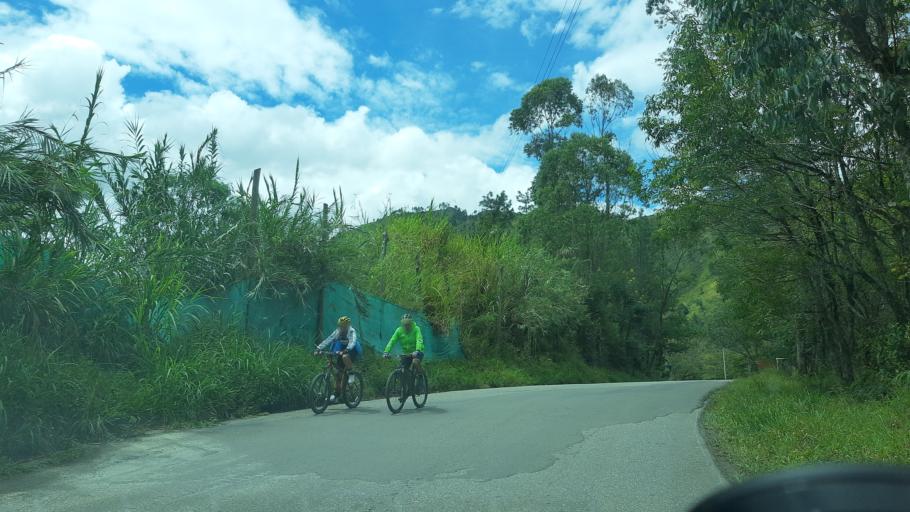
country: CO
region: Cundinamarca
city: Tenza
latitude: 5.0330
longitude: -73.3901
